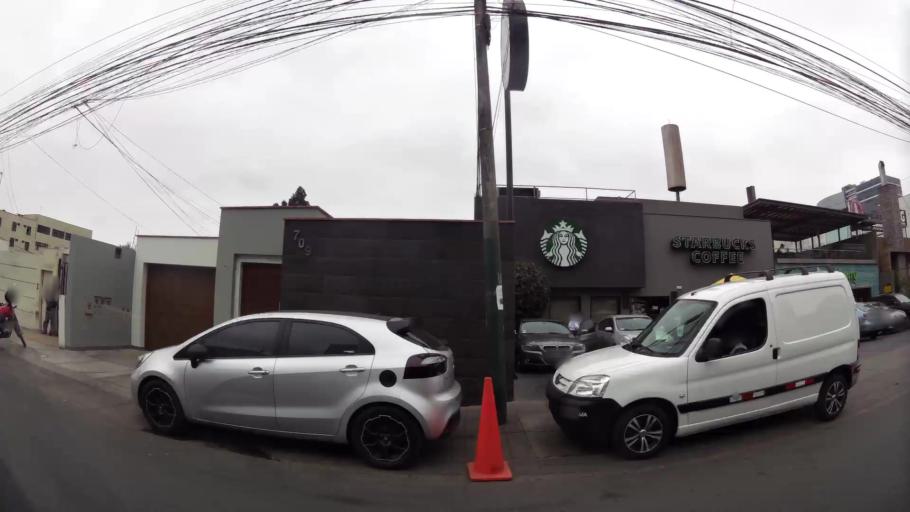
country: PE
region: Lima
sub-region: Lima
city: La Molina
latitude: -12.1013
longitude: -76.9718
